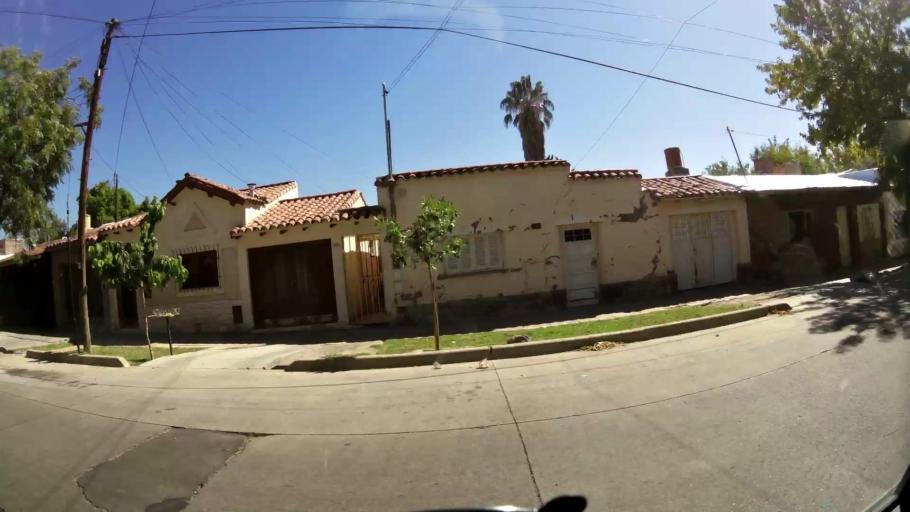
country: AR
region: Mendoza
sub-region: Departamento de Godoy Cruz
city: Godoy Cruz
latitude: -32.9064
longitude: -68.8576
